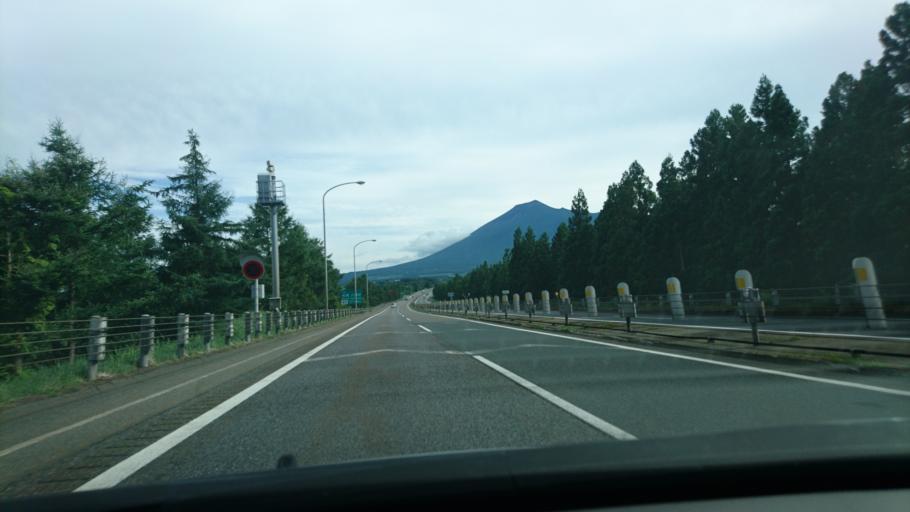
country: JP
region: Iwate
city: Shizukuishi
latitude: 39.9578
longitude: 141.0324
